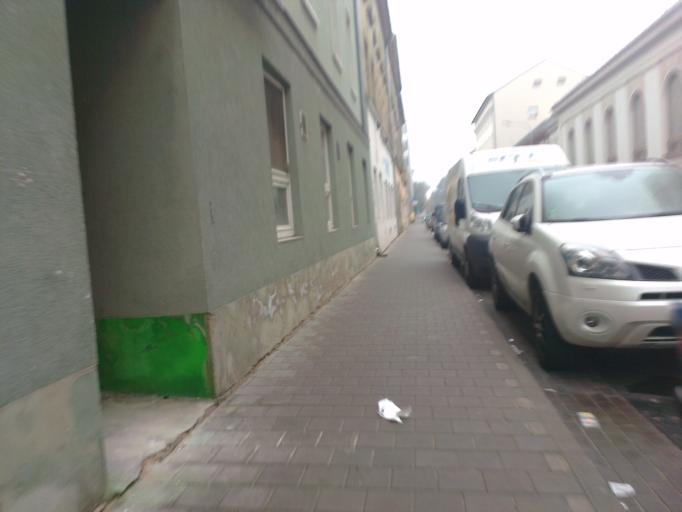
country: CZ
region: South Moravian
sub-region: Mesto Brno
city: Brno
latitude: 49.1911
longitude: 16.6209
